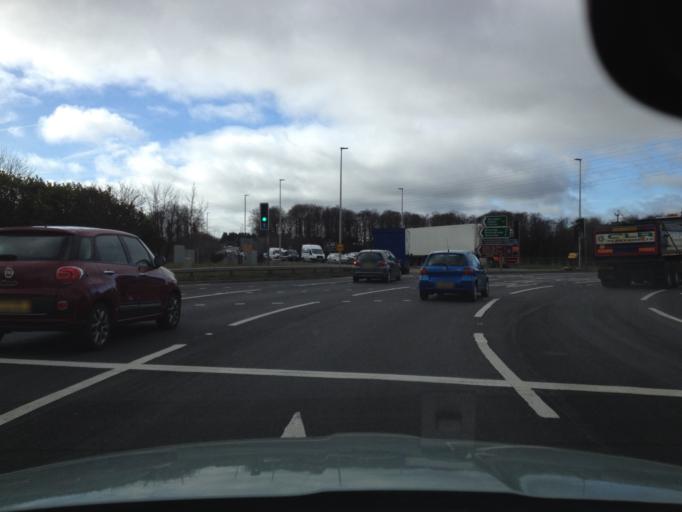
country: GB
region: Scotland
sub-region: Midlothian
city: Dalkeith
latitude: 55.8999
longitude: -3.0916
